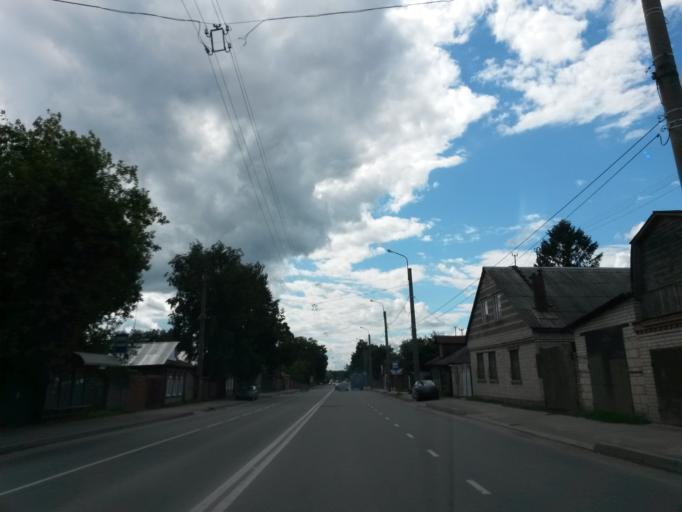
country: RU
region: Ivanovo
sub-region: Gorod Ivanovo
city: Ivanovo
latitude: 56.9916
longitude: 40.9636
